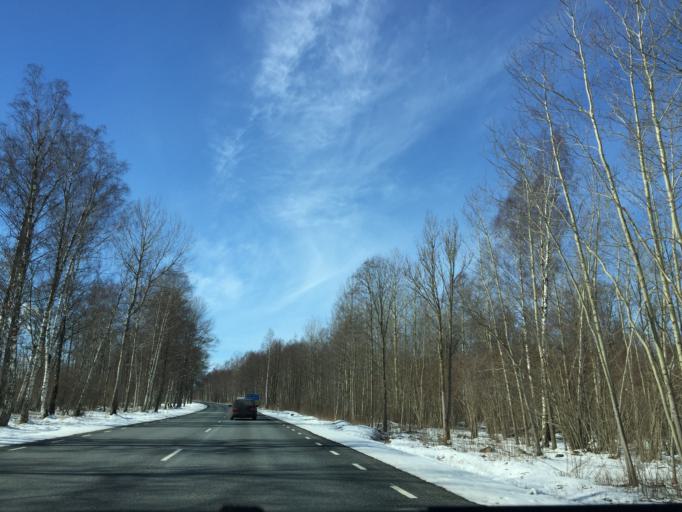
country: EE
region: Saare
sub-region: Orissaare vald
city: Orissaare
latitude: 58.6071
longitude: 23.2910
